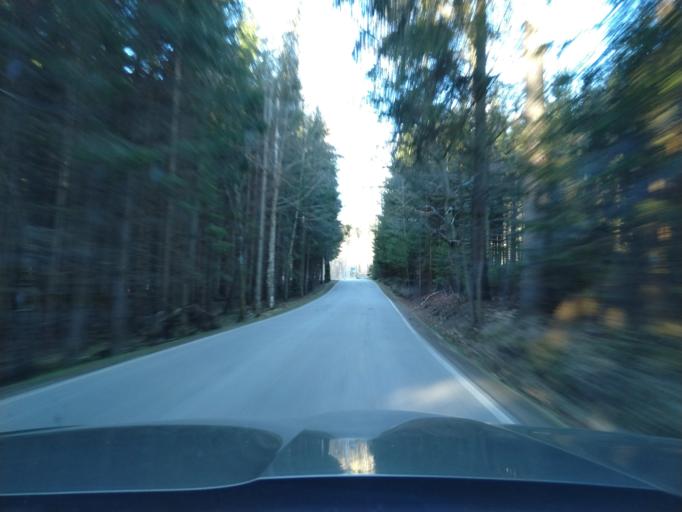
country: DE
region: Bavaria
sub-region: Lower Bavaria
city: Haidmuhle
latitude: 48.8970
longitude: 13.8090
